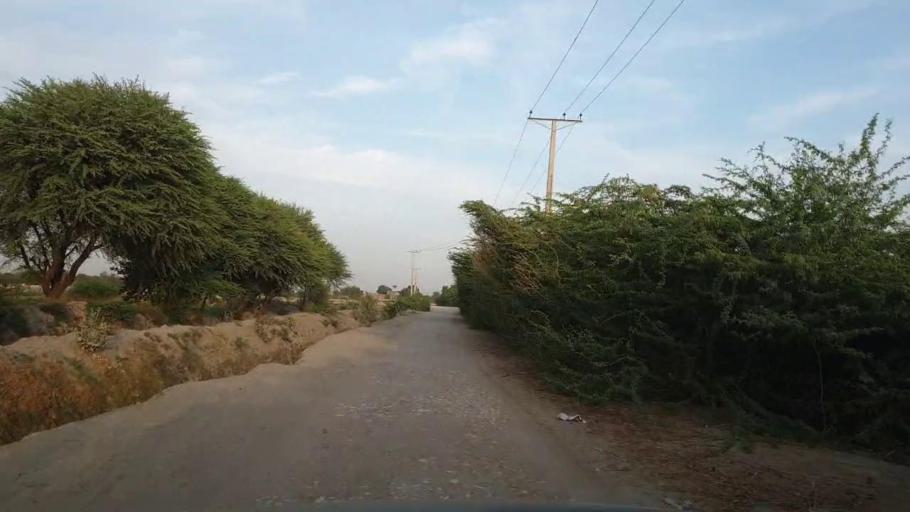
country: PK
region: Sindh
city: Kunri
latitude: 25.1608
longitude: 69.5600
